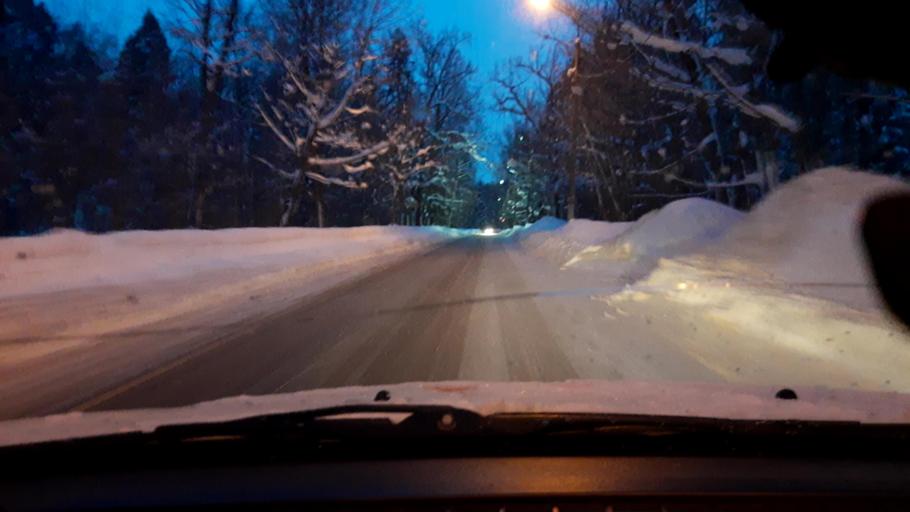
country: RU
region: Nizjnij Novgorod
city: Afonino
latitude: 56.1736
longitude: 44.0721
